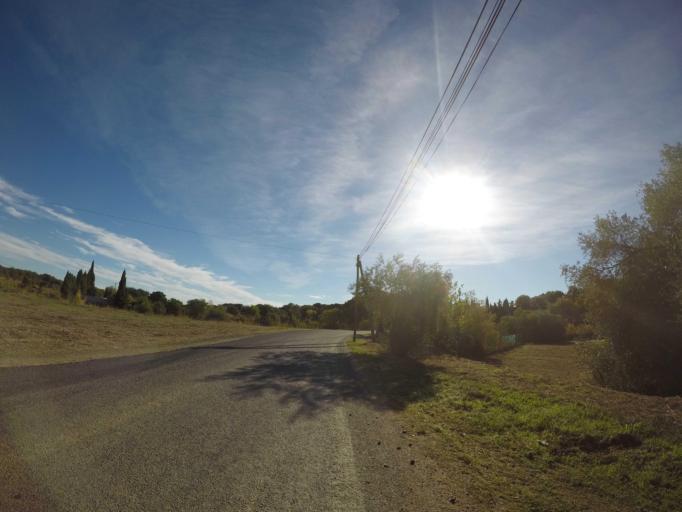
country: FR
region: Languedoc-Roussillon
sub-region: Departement des Pyrenees-Orientales
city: Llupia
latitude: 42.5823
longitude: 2.7742
